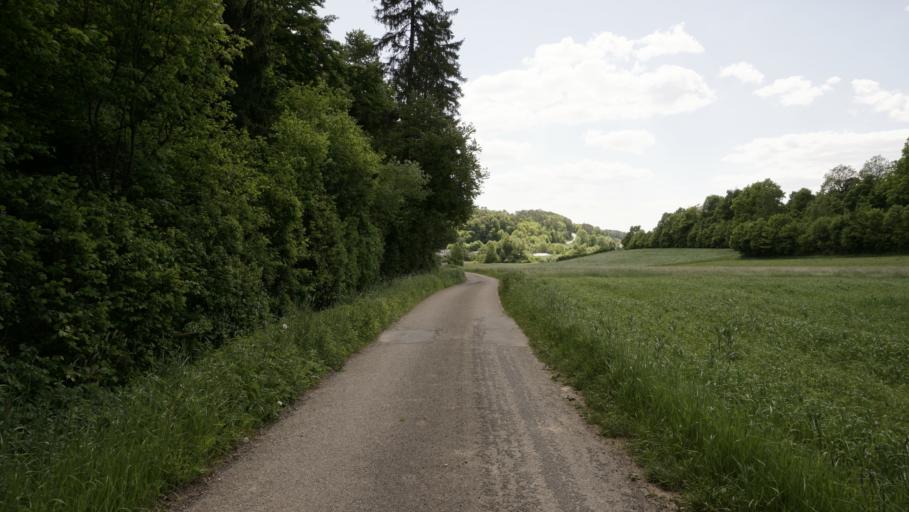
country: DE
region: Baden-Wuerttemberg
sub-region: Karlsruhe Region
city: Billigheim
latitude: 49.3870
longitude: 9.2096
